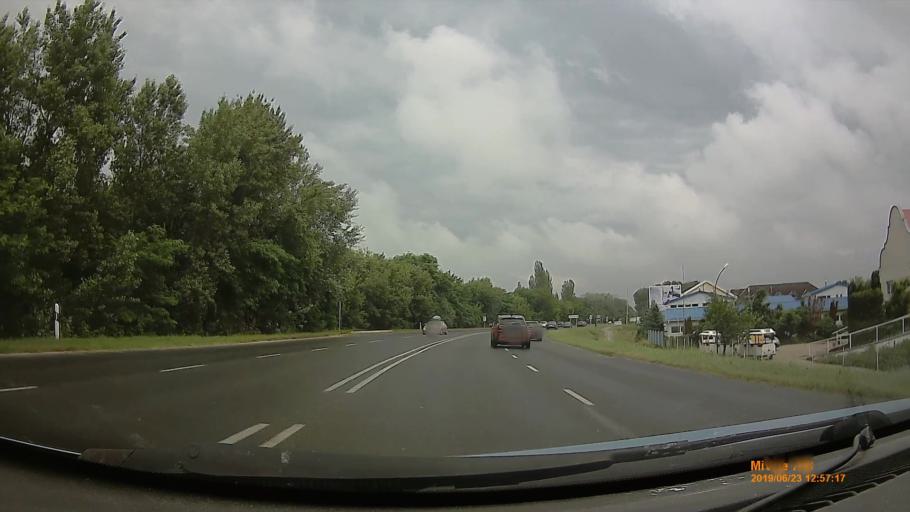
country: HU
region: Somogy
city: Siofok
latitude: 46.9145
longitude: 18.0758
